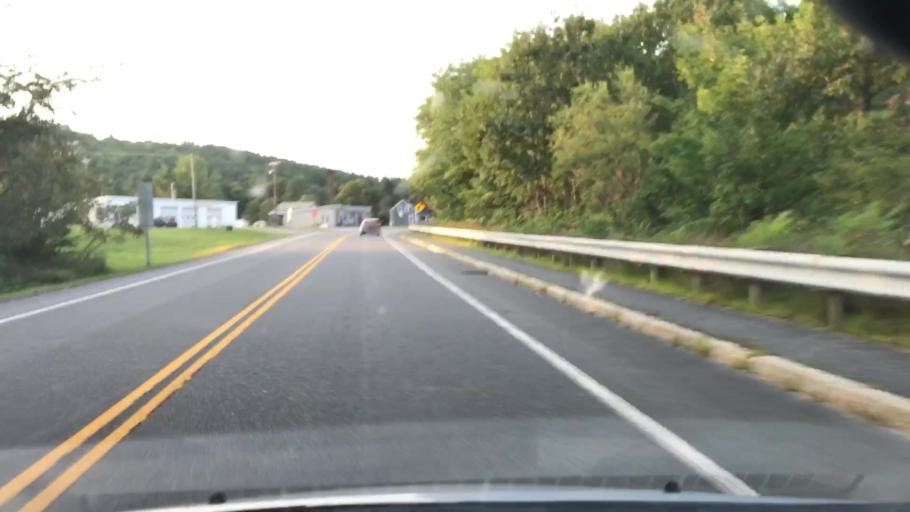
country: US
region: New Hampshire
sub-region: Grafton County
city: Rumney
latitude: 43.9245
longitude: -71.8905
